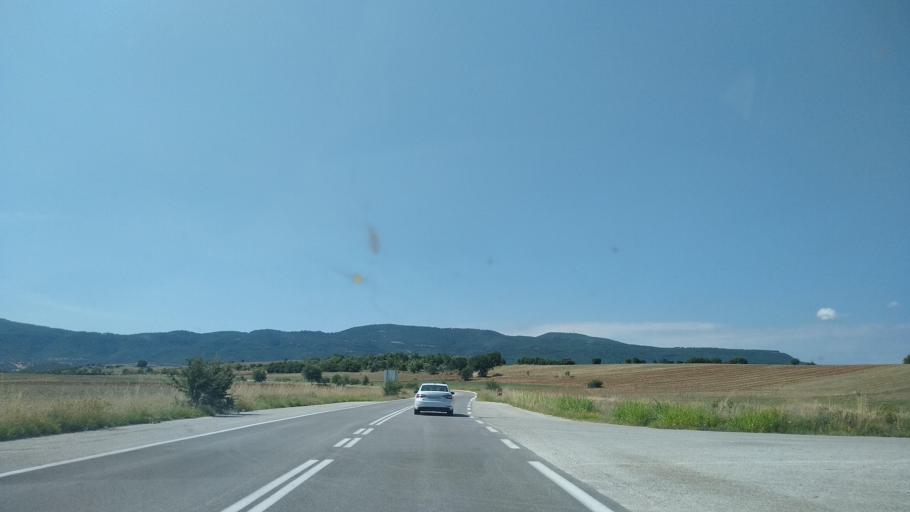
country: GR
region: Central Macedonia
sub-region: Nomos Thessalonikis
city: Nea Apollonia
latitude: 40.5307
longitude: 23.4707
